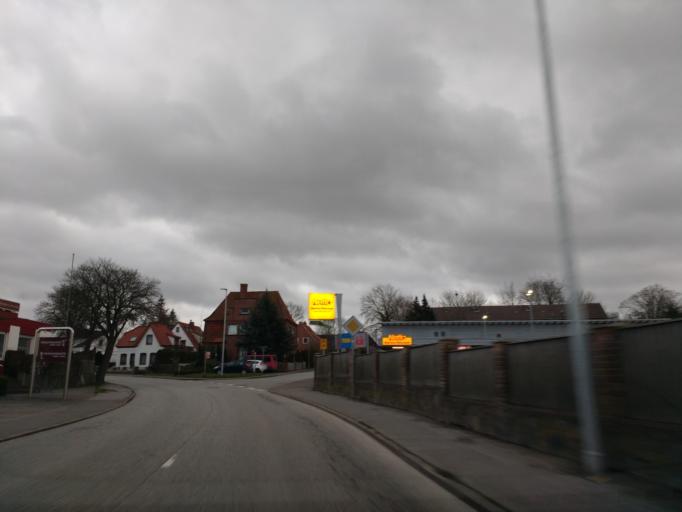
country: DE
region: Schleswig-Holstein
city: Heiligenhafen
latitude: 54.3712
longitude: 10.9870
